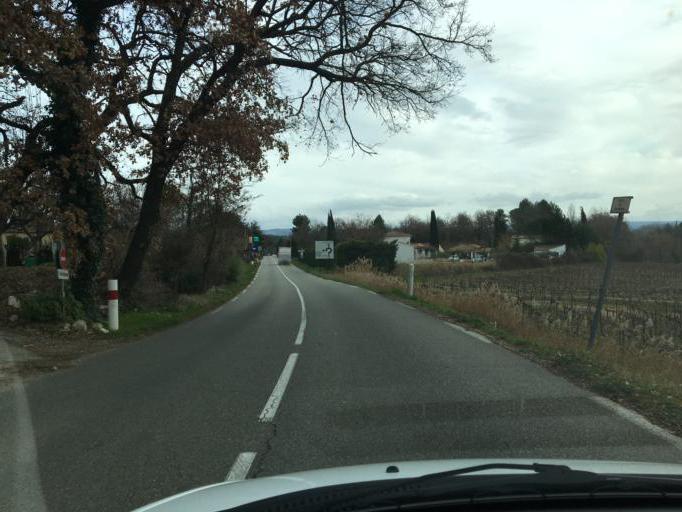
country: FR
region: Provence-Alpes-Cote d'Azur
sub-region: Departement du Vaucluse
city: Mormoiron
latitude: 44.0595
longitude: 5.1774
